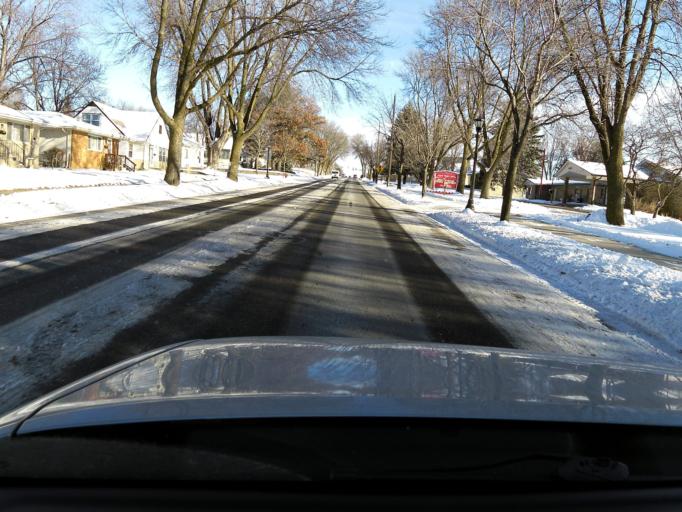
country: US
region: Minnesota
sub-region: Ramsey County
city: Maplewood
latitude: 44.9630
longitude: -93.0086
